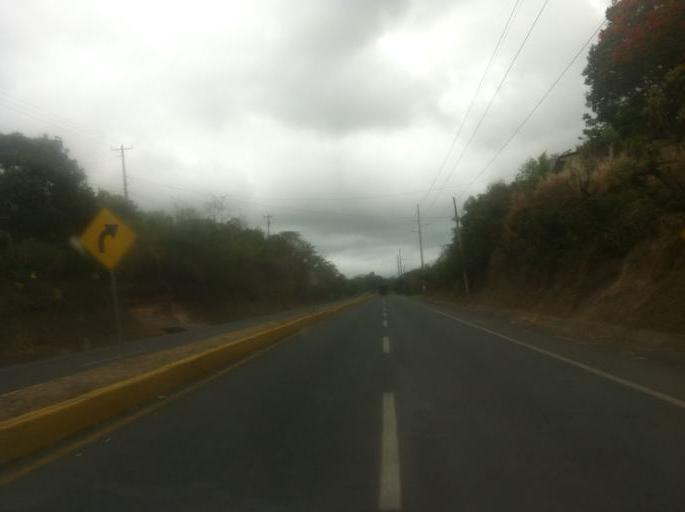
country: NI
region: Masaya
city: Masaya
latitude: 11.9738
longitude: -86.0284
